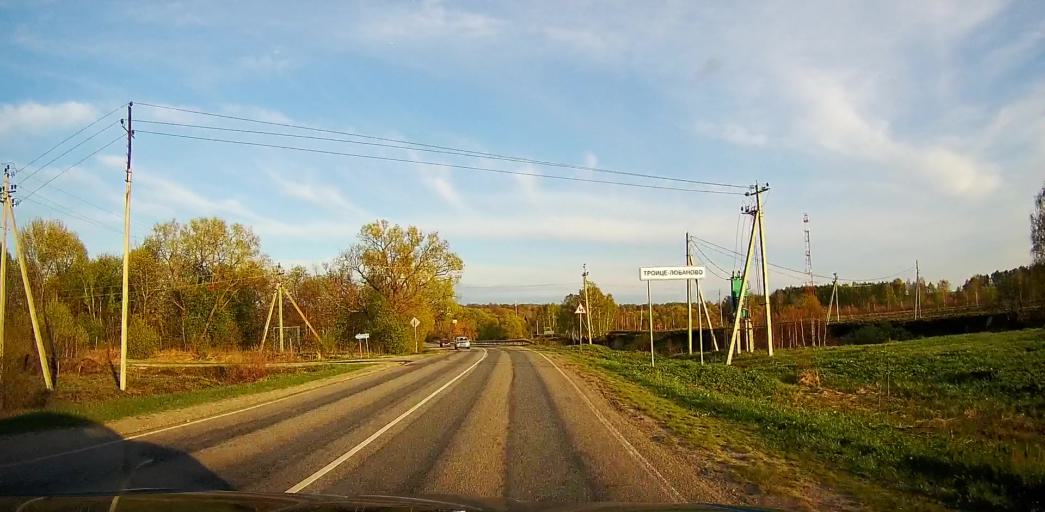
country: RU
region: Moskovskaya
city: Meshcherino
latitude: 55.2581
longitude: 38.2681
